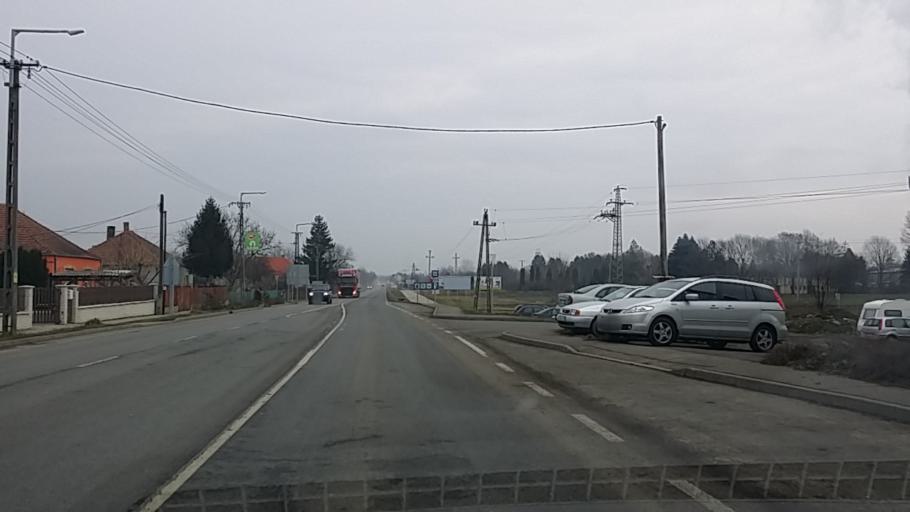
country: HU
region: Baranya
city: Mohacs
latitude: 46.0270
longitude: 18.6677
